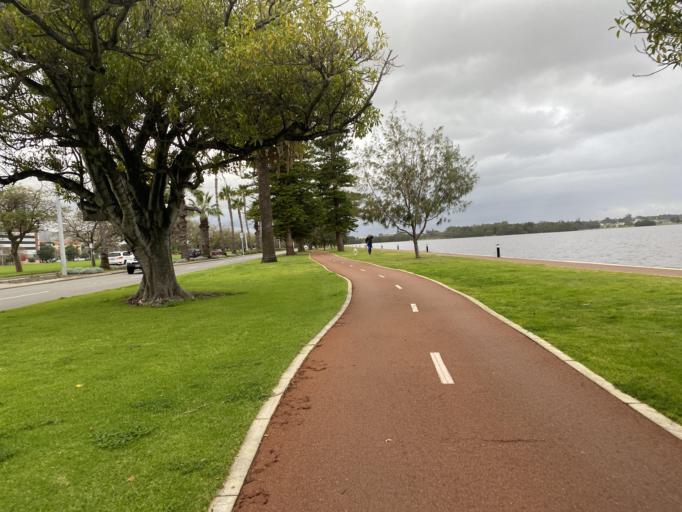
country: AU
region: Western Australia
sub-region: City of Perth
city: East Perth
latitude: -31.9625
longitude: 115.8693
